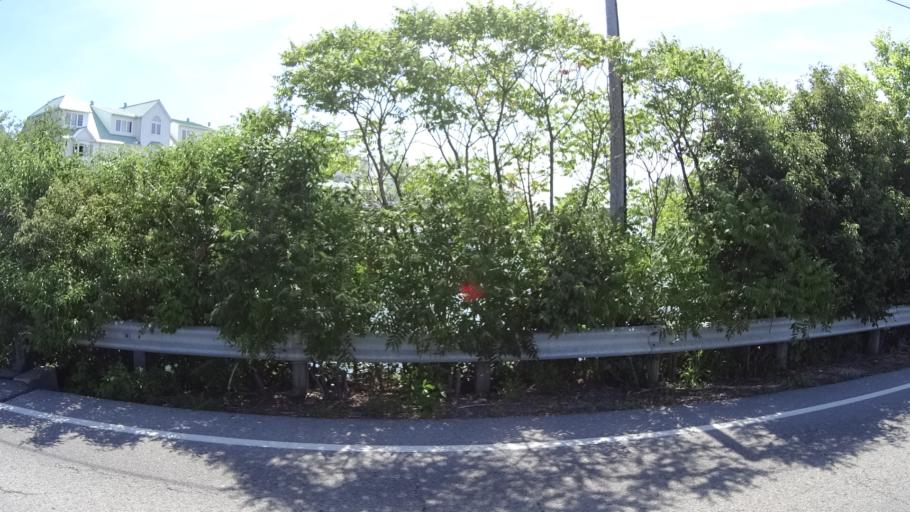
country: US
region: Ohio
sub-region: Erie County
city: Huron
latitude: 41.4324
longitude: -82.6212
